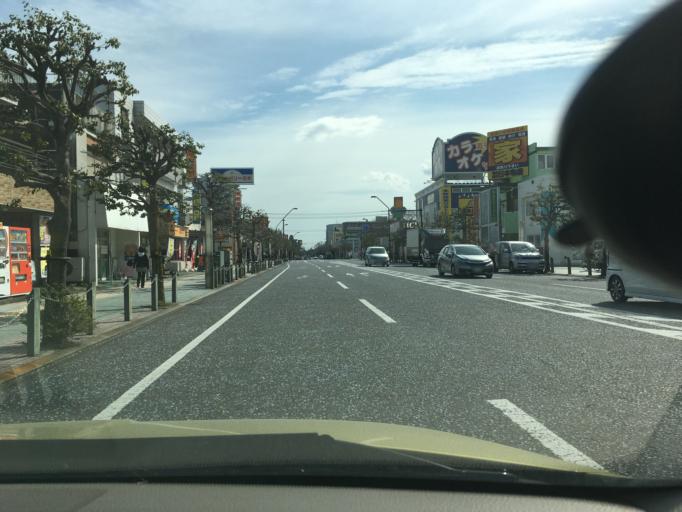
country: JP
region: Kanagawa
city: Zama
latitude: 35.5731
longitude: 139.3684
